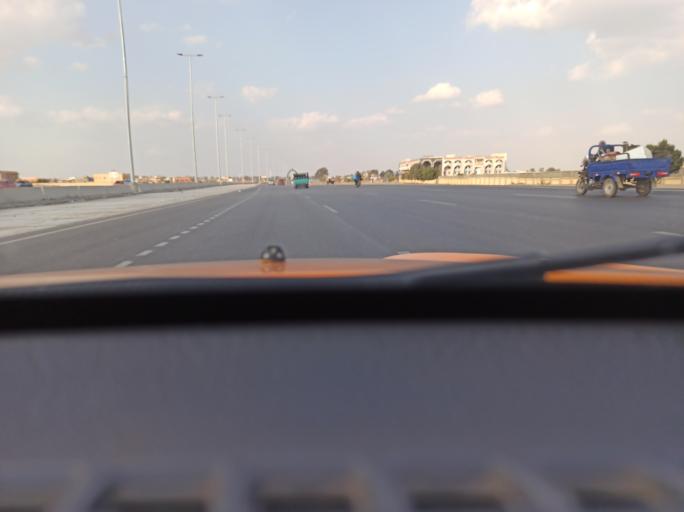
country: EG
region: Al Isma'iliyah
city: Ismailia
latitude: 30.6027
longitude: 32.2098
